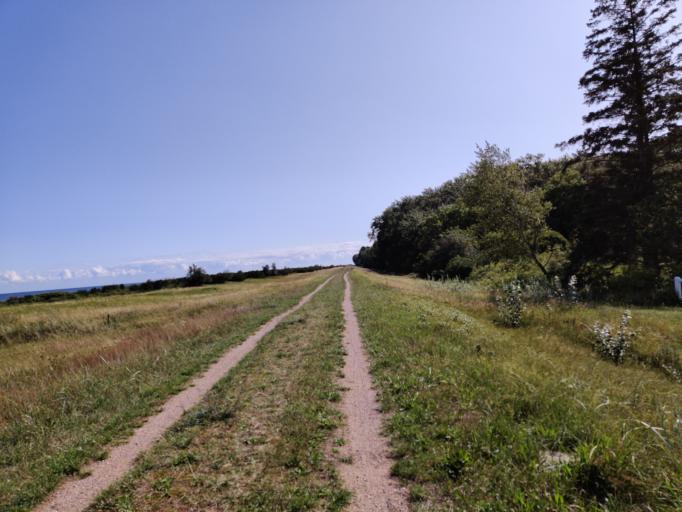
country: DK
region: Zealand
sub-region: Guldborgsund Kommune
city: Nykobing Falster
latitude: 54.6127
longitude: 11.9649
